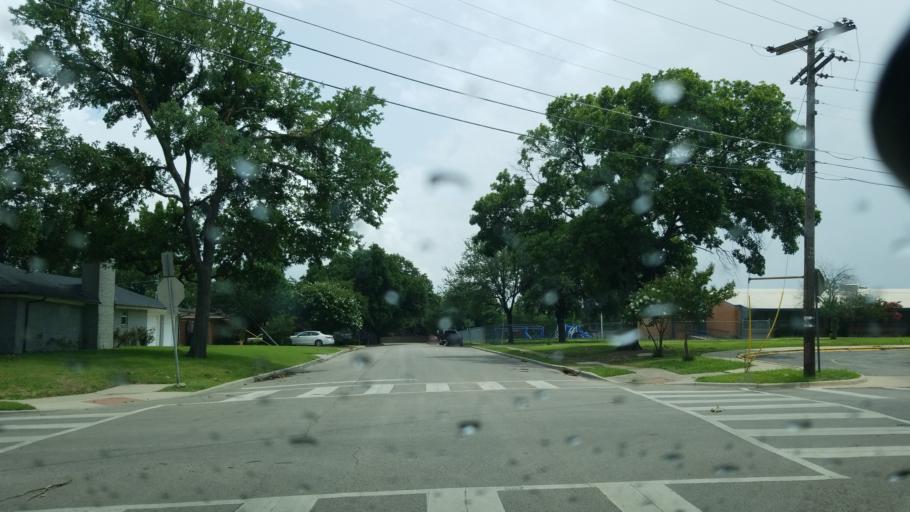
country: US
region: Texas
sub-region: Dallas County
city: Farmers Branch
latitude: 32.8773
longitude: -96.8676
